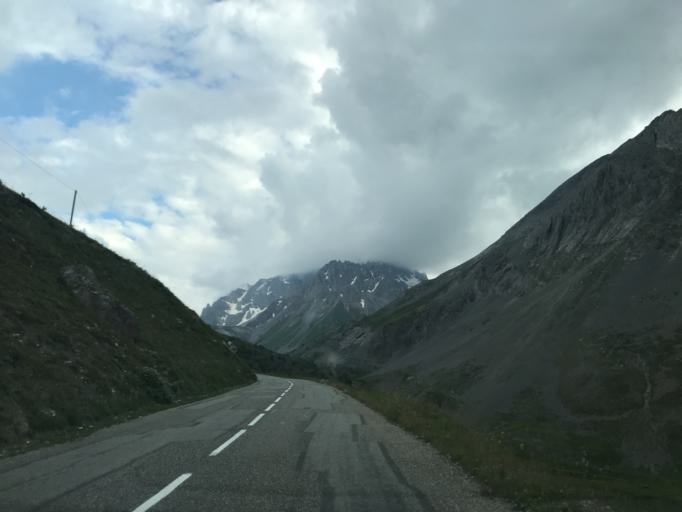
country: FR
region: Rhone-Alpes
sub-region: Departement de la Savoie
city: Valloire
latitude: 45.1064
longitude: 6.4255
